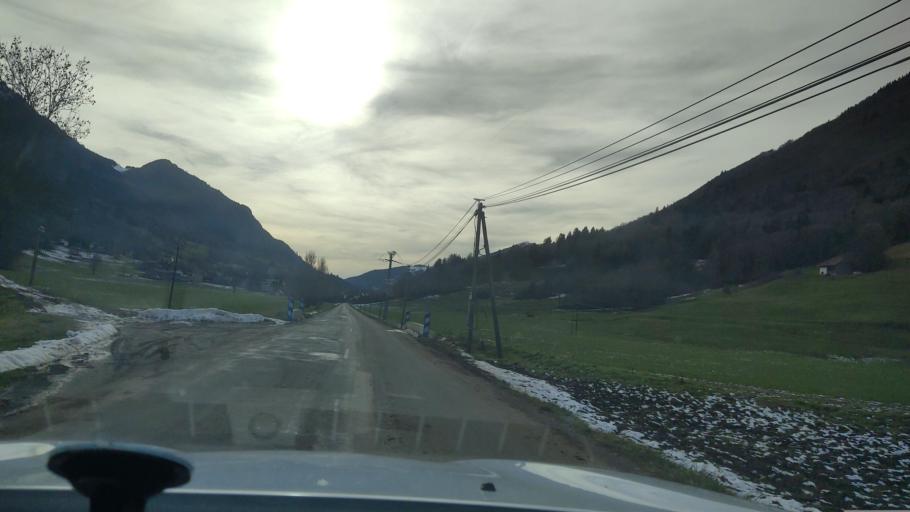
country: FR
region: Rhone-Alpes
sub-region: Departement de la Savoie
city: Gresy-sur-Isere
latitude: 45.6405
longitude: 6.1620
